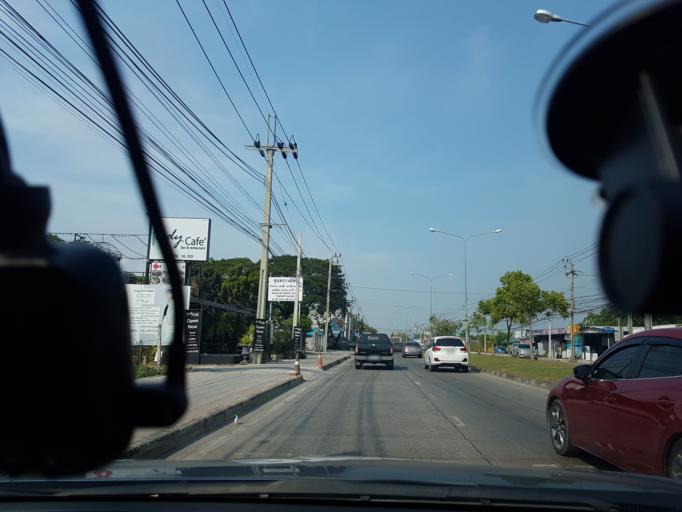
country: TH
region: Bangkok
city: Khlong Sam Wa
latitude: 13.8698
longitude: 100.7224
